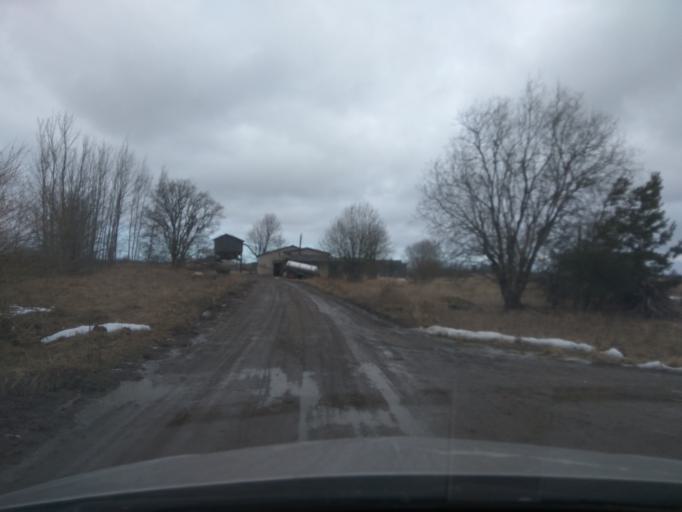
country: LV
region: Ventspils
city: Ventspils
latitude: 57.3333
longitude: 21.6459
